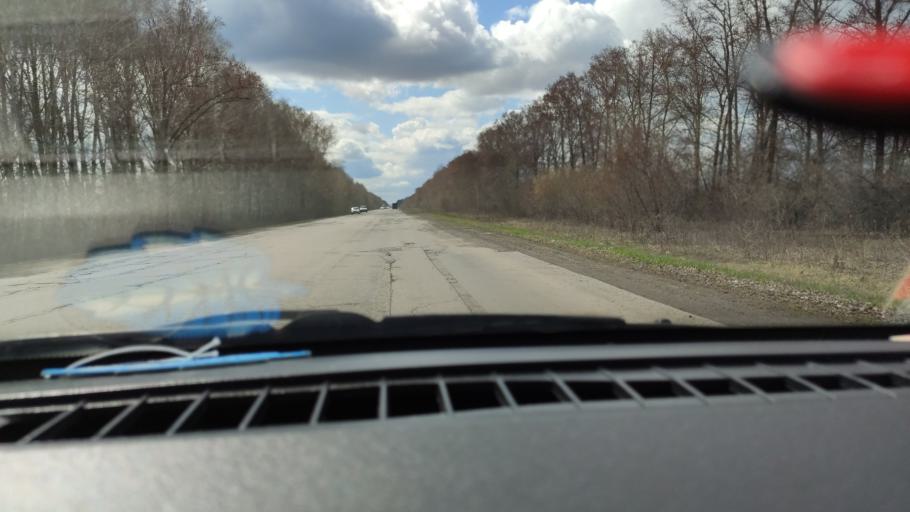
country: RU
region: Samara
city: Tol'yatti
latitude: 53.6437
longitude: 49.4210
